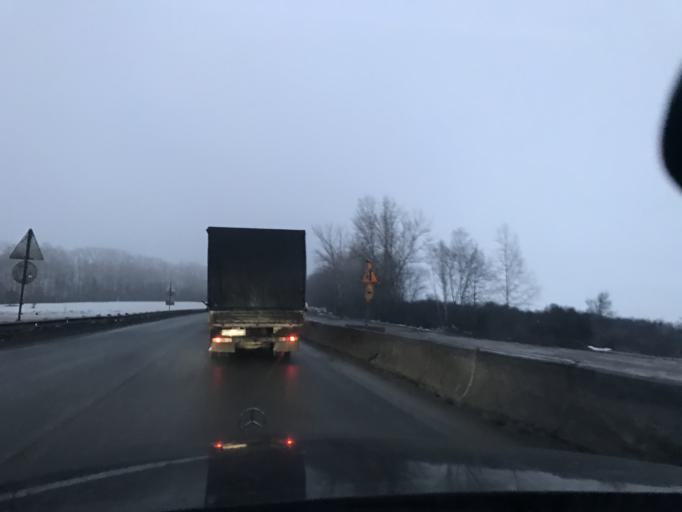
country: RU
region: Vladimir
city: Novovyazniki
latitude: 56.2166
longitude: 42.2417
